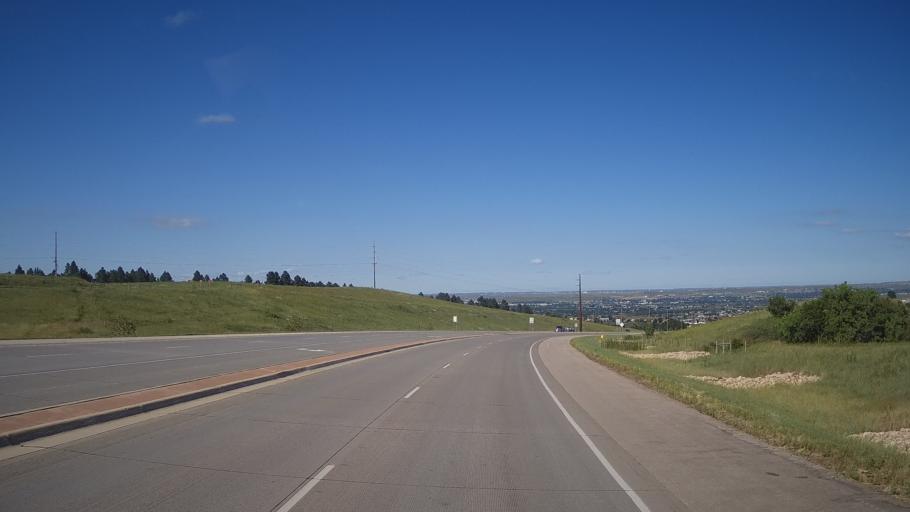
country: US
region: South Dakota
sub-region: Pennington County
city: Rapid City
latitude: 44.0204
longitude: -103.2414
